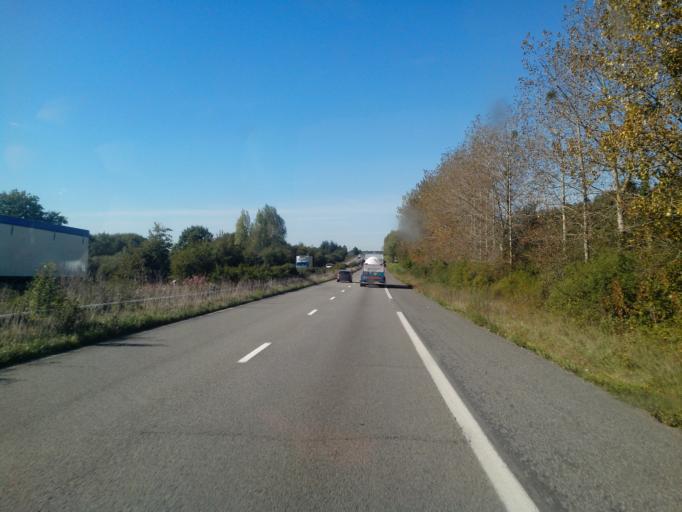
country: FR
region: Pays de la Loire
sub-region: Departement de la Loire-Atlantique
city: Missillac
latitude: 47.4616
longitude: -2.1496
